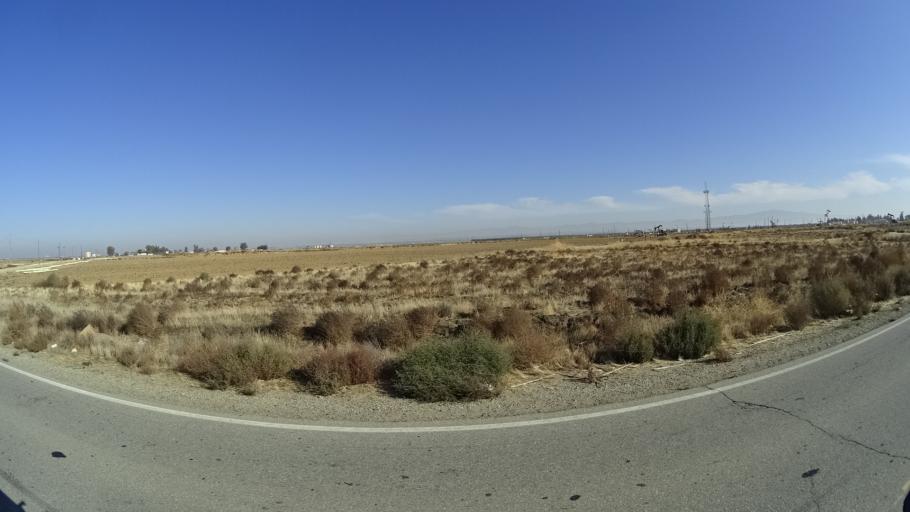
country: US
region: California
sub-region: Kern County
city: Rosedale
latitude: 35.4313
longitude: -119.1497
